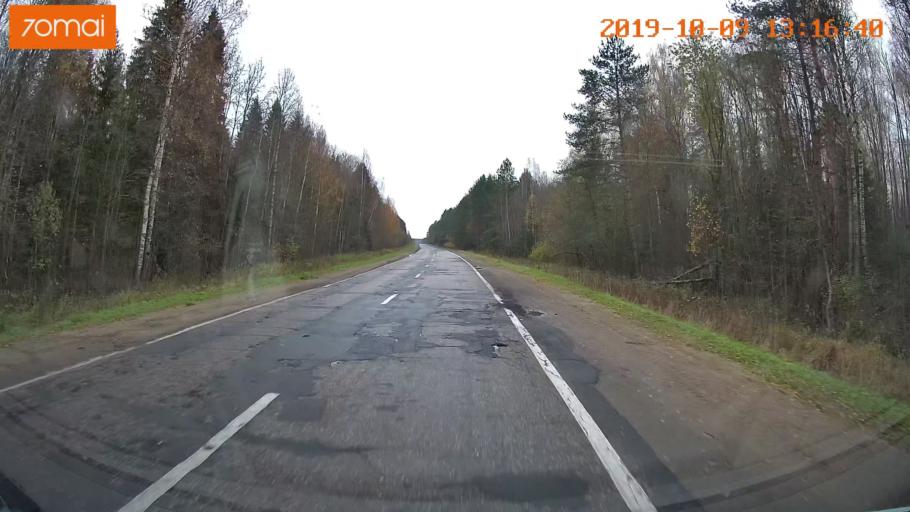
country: RU
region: Jaroslavl
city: Lyubim
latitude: 58.3596
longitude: 40.7689
